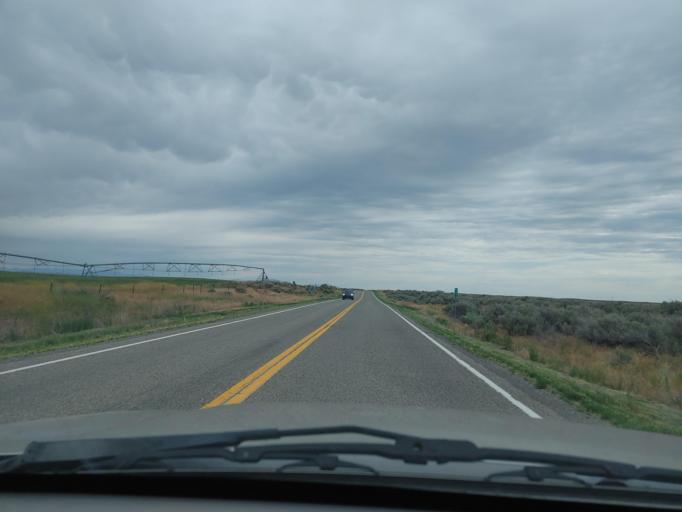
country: US
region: Idaho
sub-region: Lincoln County
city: Shoshone
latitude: 43.0630
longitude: -114.1236
